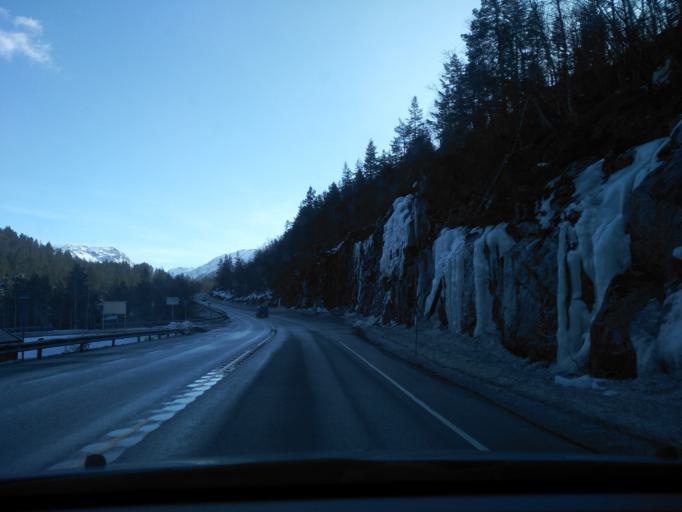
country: NO
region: Hordaland
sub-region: Odda
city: Odda
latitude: 59.9111
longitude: 6.6104
